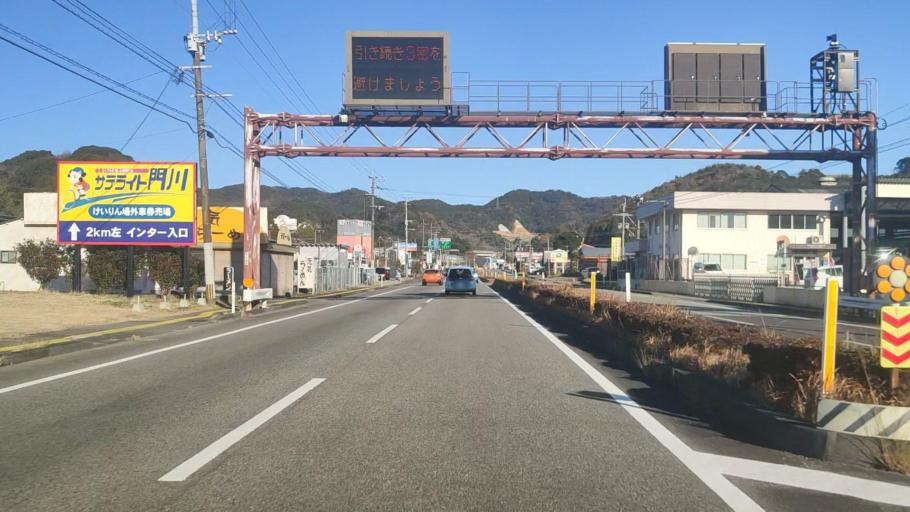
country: JP
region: Miyazaki
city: Nobeoka
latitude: 32.4920
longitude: 131.6635
